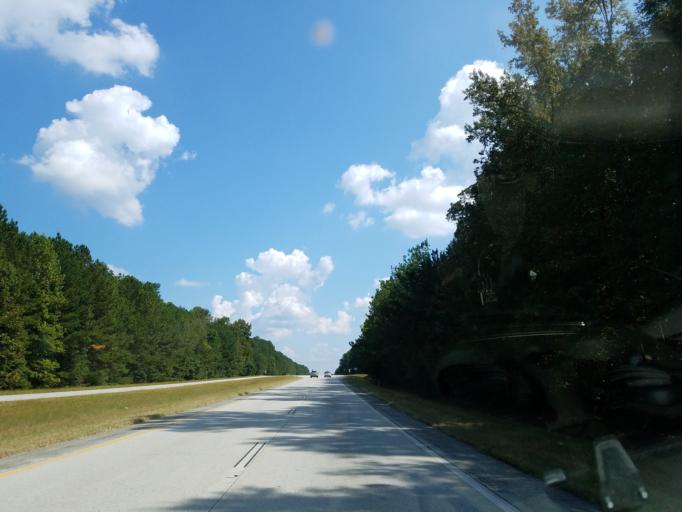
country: US
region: Georgia
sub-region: Barrow County
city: Statham
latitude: 33.9596
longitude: -83.6178
